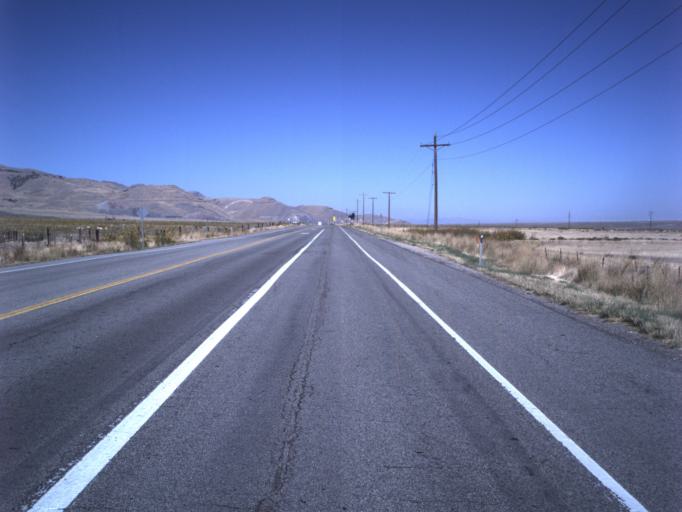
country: US
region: Utah
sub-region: Tooele County
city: Grantsville
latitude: 40.6266
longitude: -112.5092
